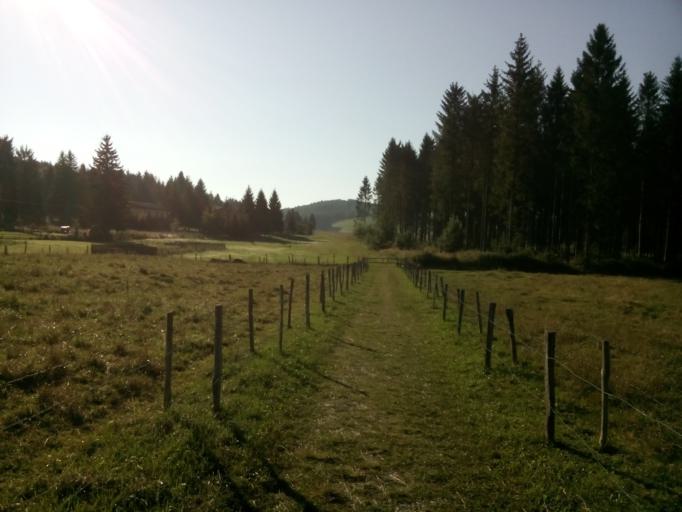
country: IT
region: Veneto
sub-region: Provincia di Vicenza
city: Conco
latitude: 45.8202
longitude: 11.6204
